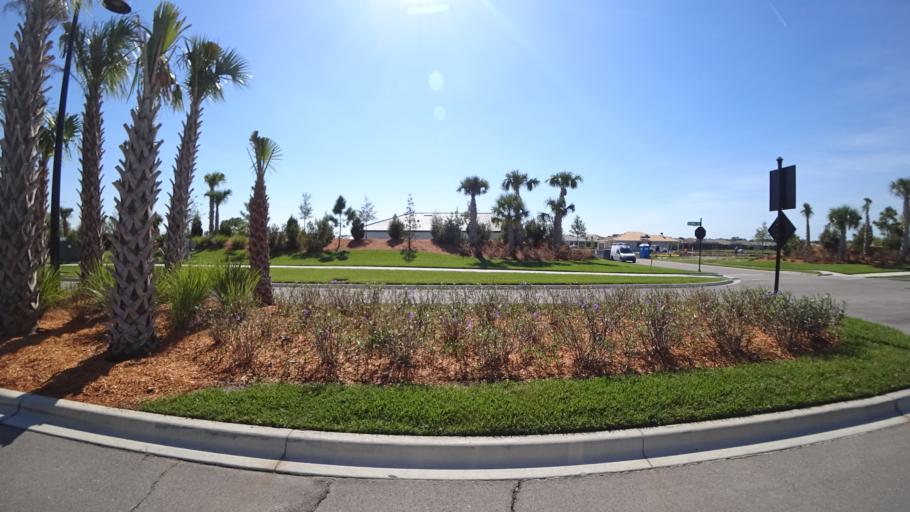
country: US
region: Florida
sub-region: Sarasota County
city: The Meadows
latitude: 27.4068
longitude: -82.3606
